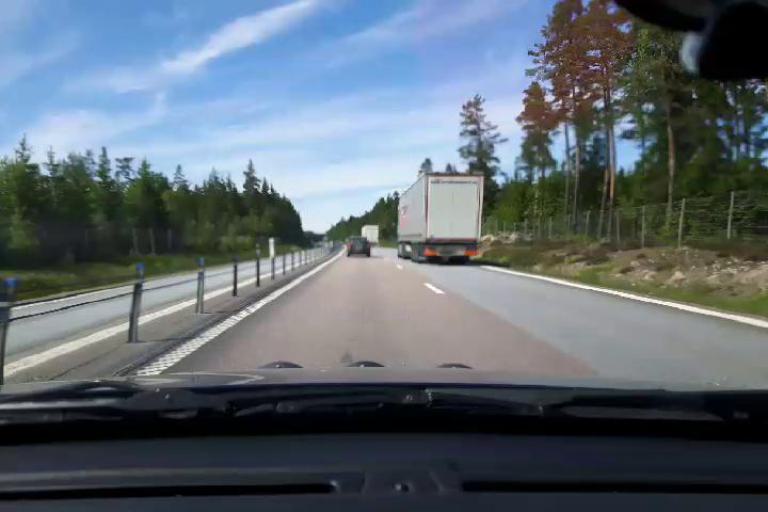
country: SE
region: Gaevleborg
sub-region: Gavle Kommun
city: Norrsundet
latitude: 60.8642
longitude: 17.0590
